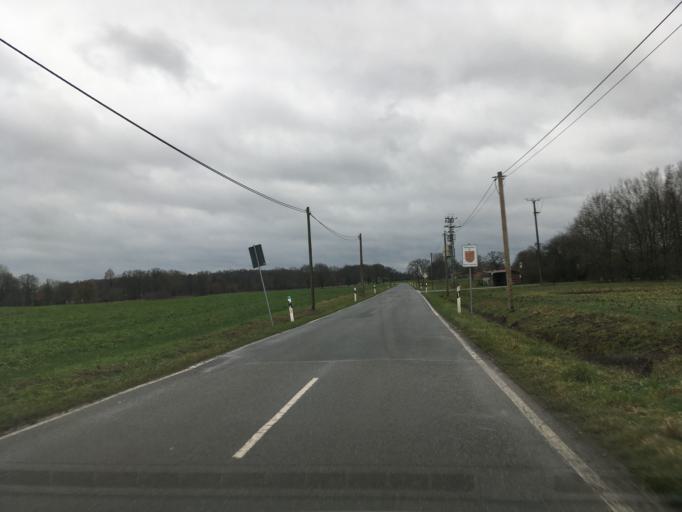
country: DE
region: North Rhine-Westphalia
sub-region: Regierungsbezirk Munster
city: Legden
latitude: 52.0451
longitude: 7.1667
